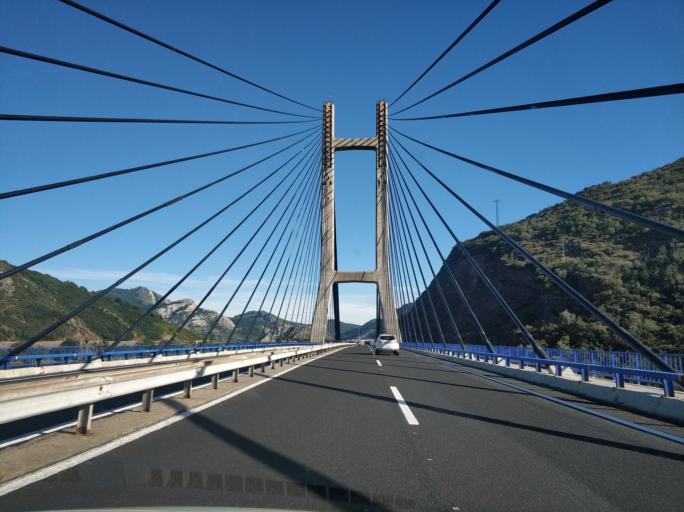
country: ES
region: Castille and Leon
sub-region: Provincia de Leon
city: Sena de Luna
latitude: 42.8957
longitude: -5.8882
